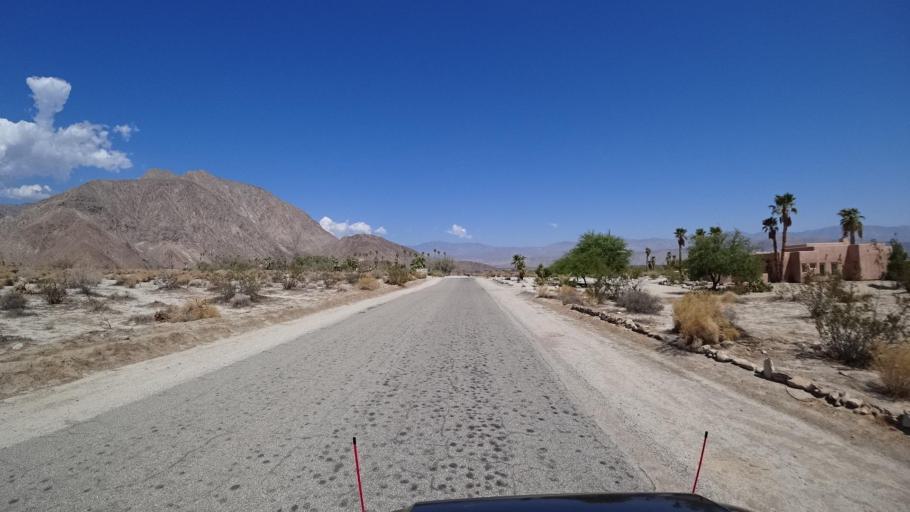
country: US
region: California
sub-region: San Diego County
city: Borrego Springs
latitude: 33.2665
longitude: -116.3996
